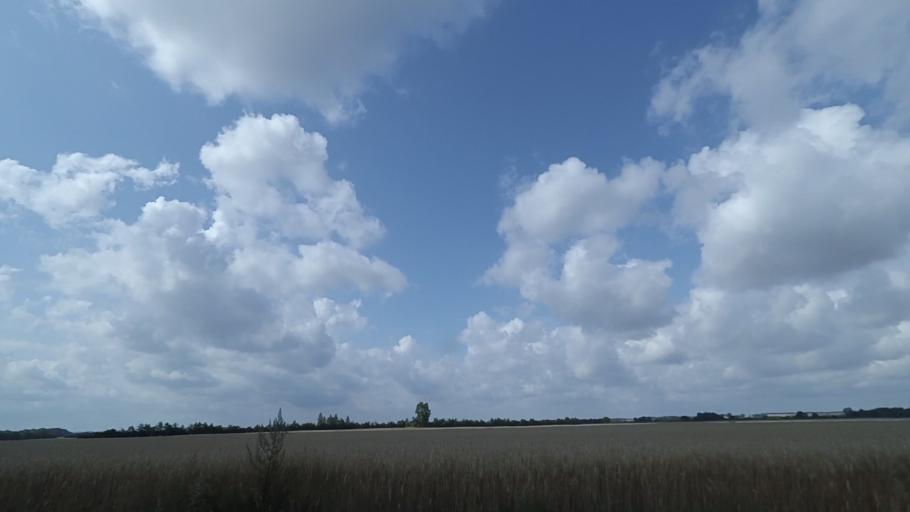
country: DK
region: Central Jutland
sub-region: Norddjurs Kommune
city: Auning
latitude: 56.5056
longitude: 10.4232
